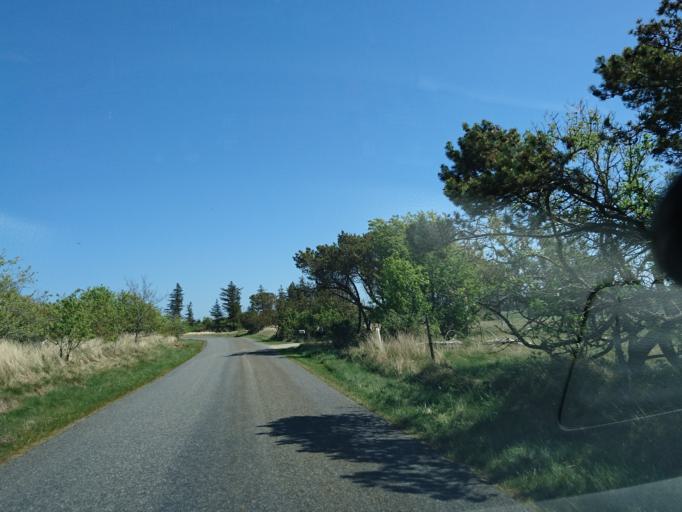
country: DK
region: North Denmark
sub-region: Frederikshavn Kommune
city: Strandby
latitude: 57.6252
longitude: 10.3797
